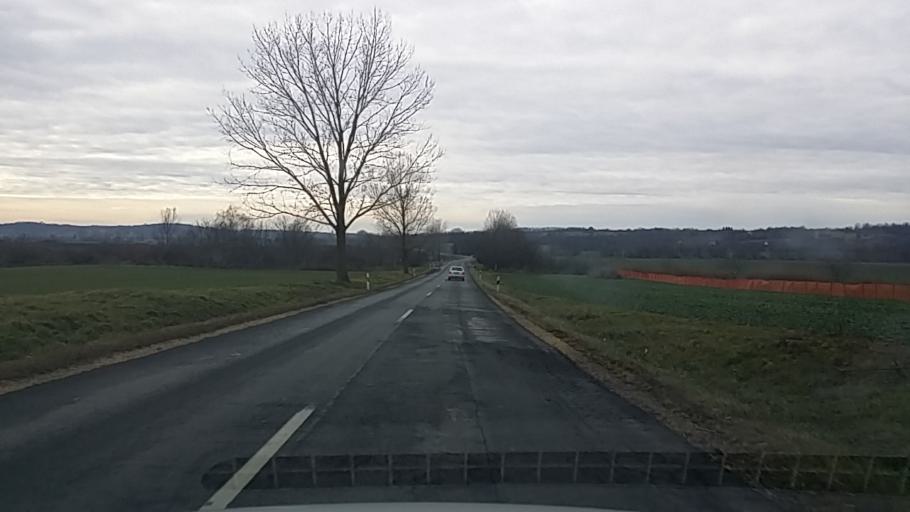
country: HU
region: Vas
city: Celldomolk
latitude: 47.2587
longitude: 17.0523
